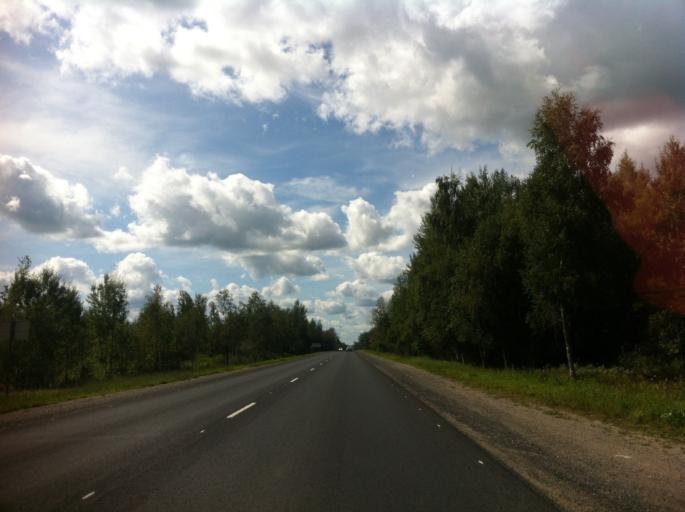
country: RU
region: Pskov
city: Izborsk
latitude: 57.7549
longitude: 28.0667
